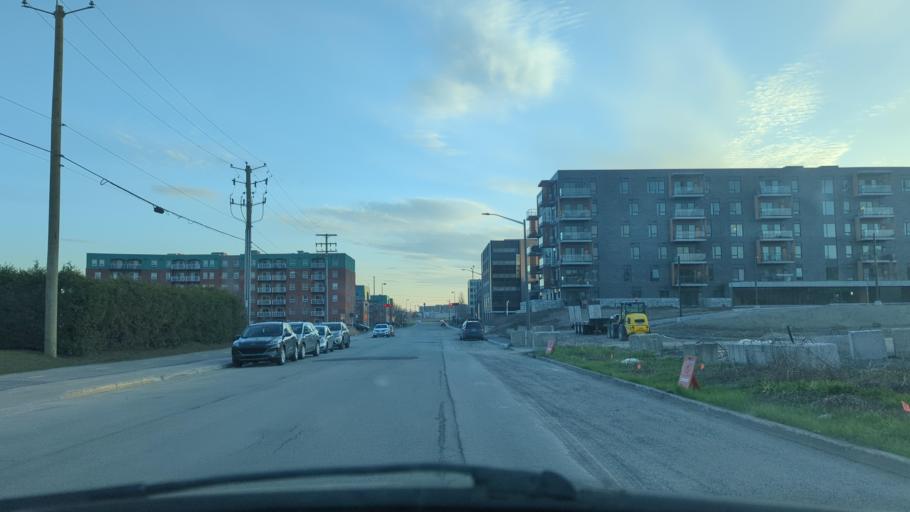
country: CA
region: Quebec
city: Quebec
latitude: 46.8469
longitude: -71.2657
